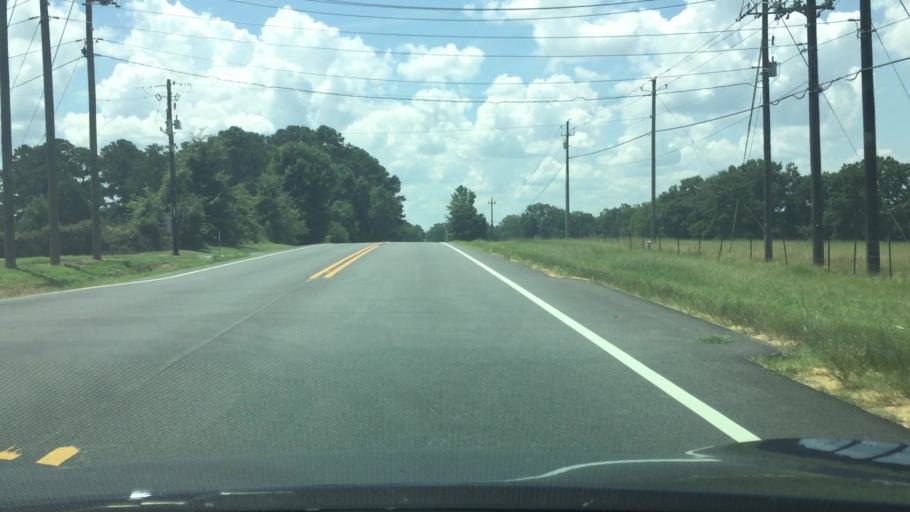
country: US
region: Alabama
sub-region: Montgomery County
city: Pike Road
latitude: 32.3322
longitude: -86.0946
